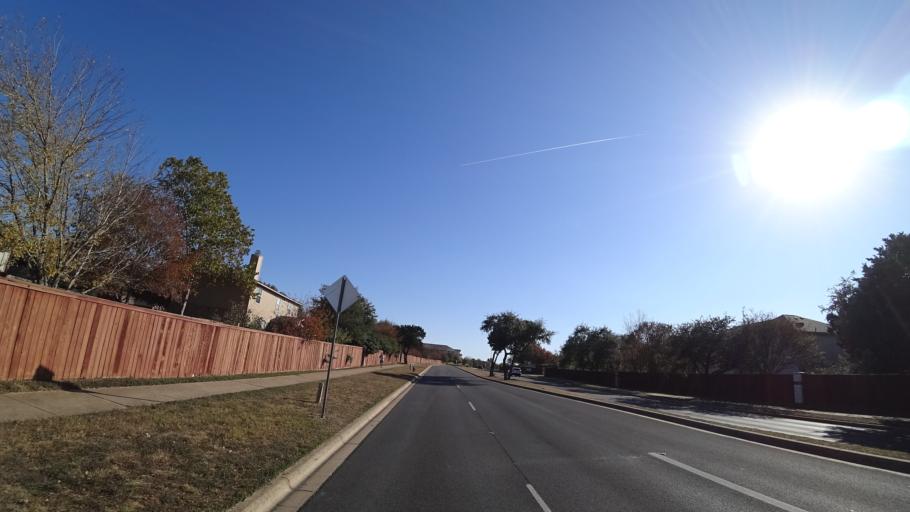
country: US
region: Texas
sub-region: Williamson County
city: Cedar Park
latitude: 30.5249
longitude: -97.8545
